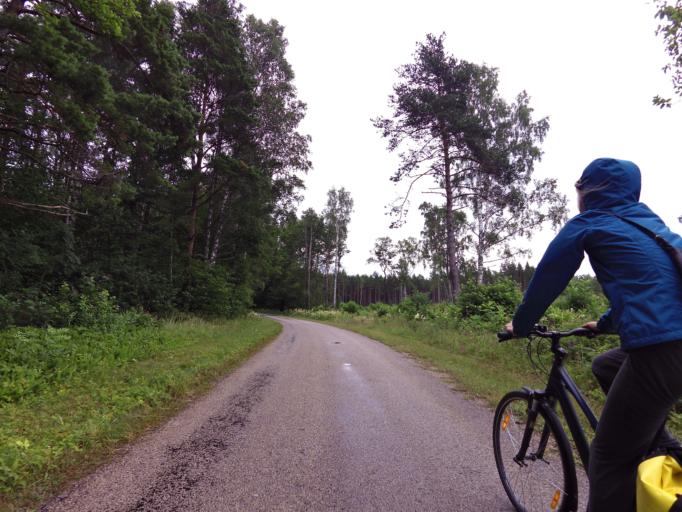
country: EE
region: Laeaene
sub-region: Vormsi vald
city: Hullo
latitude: 59.0191
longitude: 23.3234
